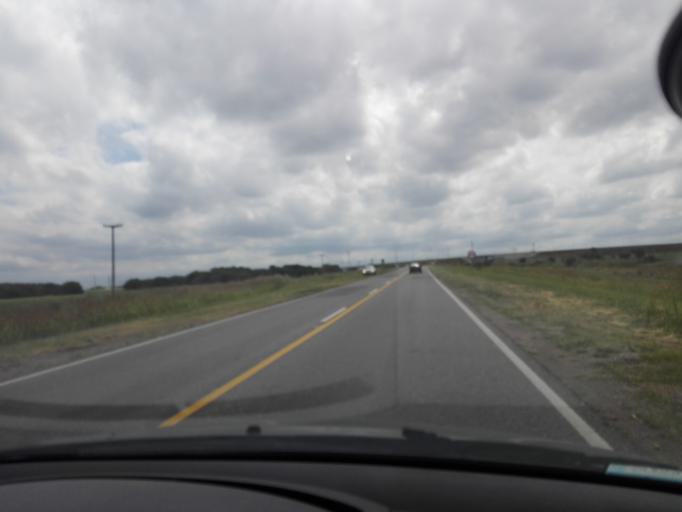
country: AR
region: Cordoba
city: Alta Gracia
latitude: -31.6520
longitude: -64.3092
